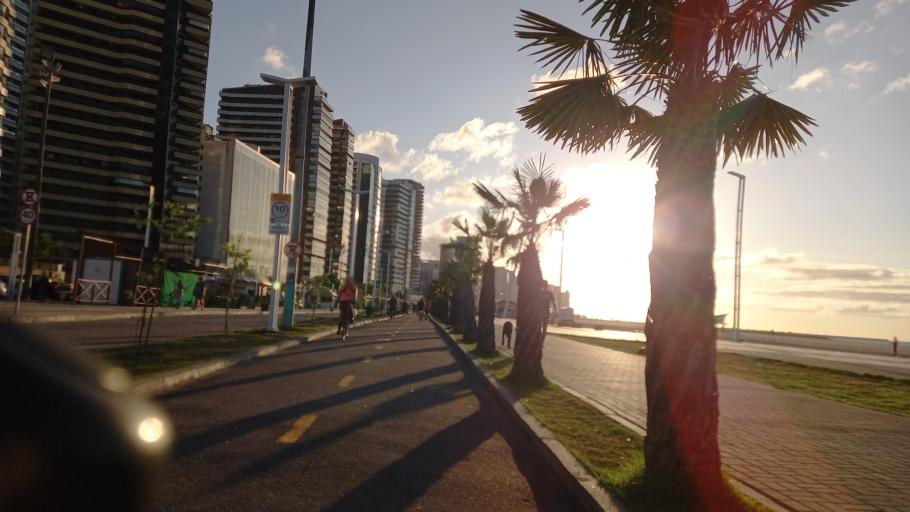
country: BR
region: Ceara
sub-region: Fortaleza
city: Fortaleza
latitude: -3.7246
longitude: -38.4991
